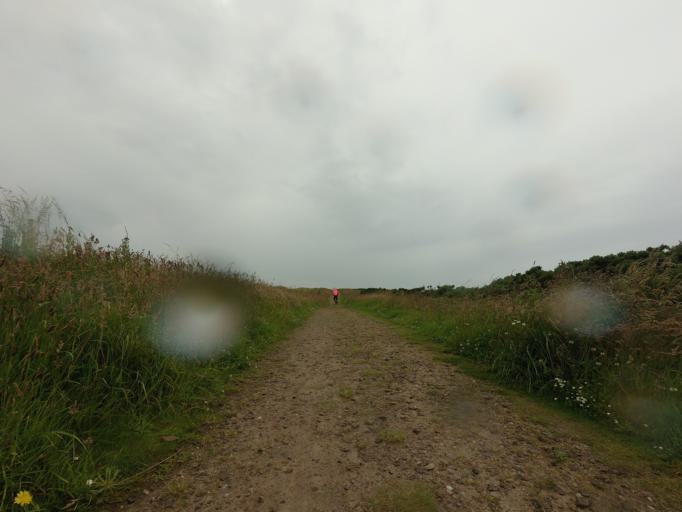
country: GB
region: Scotland
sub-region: Moray
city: Portknockie
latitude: 57.7032
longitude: -2.8780
